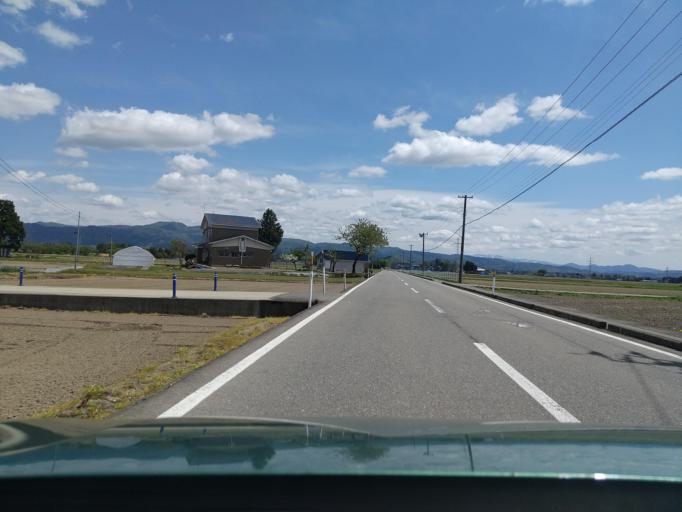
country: JP
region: Akita
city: Omagari
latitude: 39.3871
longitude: 140.5098
